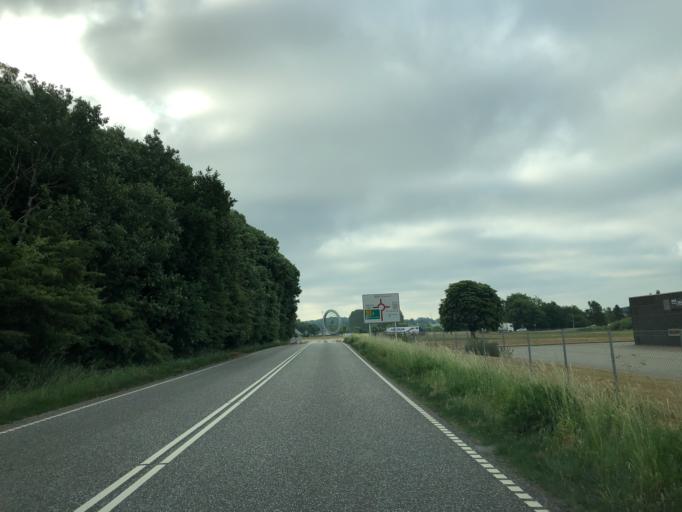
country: DK
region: South Denmark
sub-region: Vejle Kommune
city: Give
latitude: 55.8642
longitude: 9.2495
